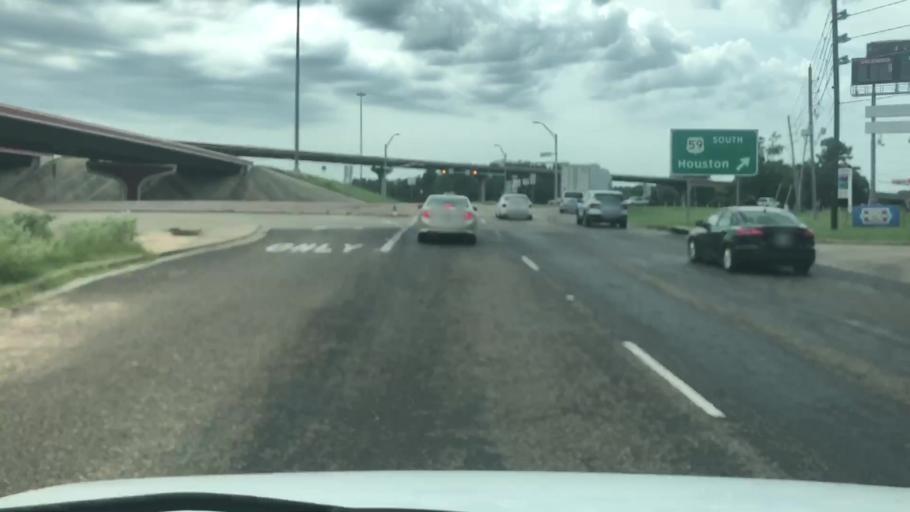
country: US
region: Texas
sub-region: Bowie County
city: Wake Village
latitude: 33.3956
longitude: -94.0987
